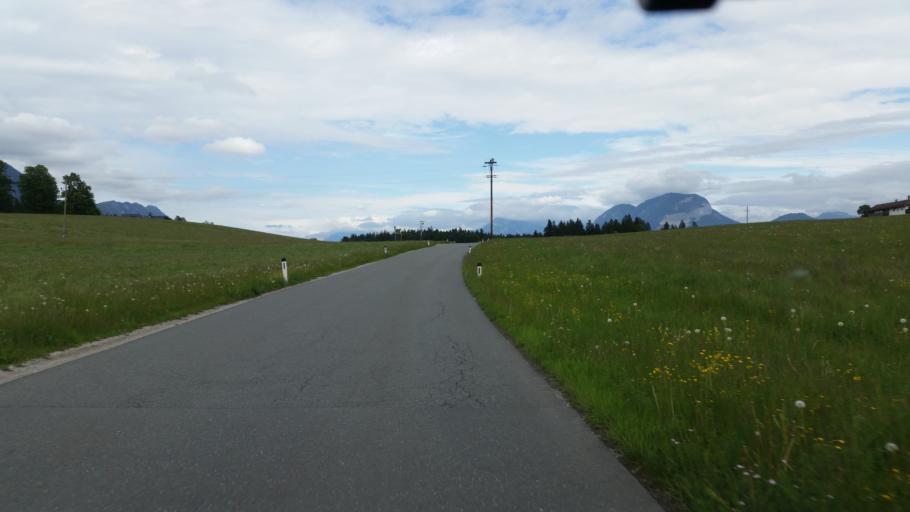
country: AT
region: Tyrol
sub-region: Politischer Bezirk Kufstein
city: Kundl
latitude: 47.4916
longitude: 12.0064
